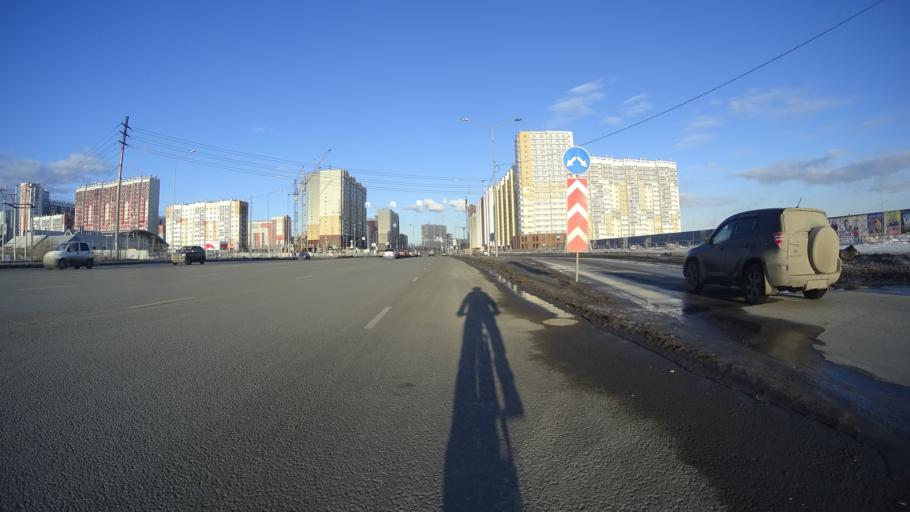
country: RU
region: Chelyabinsk
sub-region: Gorod Chelyabinsk
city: Chelyabinsk
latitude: 55.1690
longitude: 61.3065
